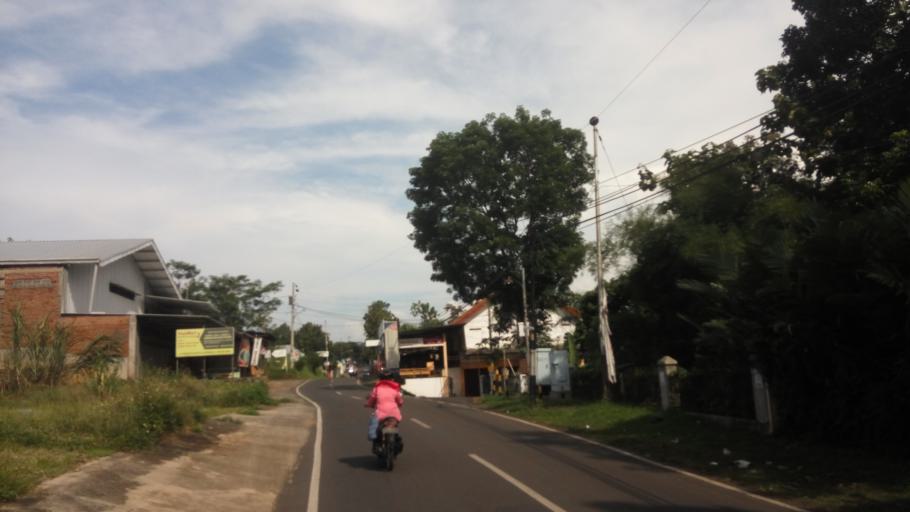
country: ID
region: Central Java
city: Ungaran
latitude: -7.1442
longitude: 110.4181
